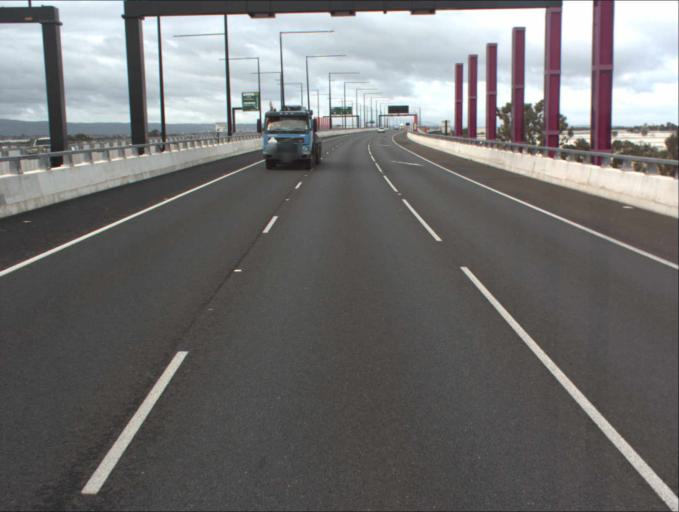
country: AU
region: South Australia
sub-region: Port Adelaide Enfield
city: Blair Athol
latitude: -34.8366
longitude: 138.5631
